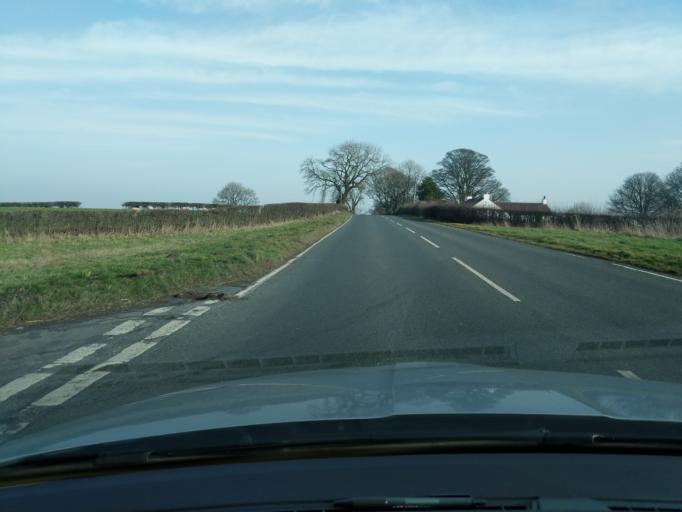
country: GB
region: England
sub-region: North Yorkshire
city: Catterick Garrison
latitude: 54.3462
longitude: -1.7164
